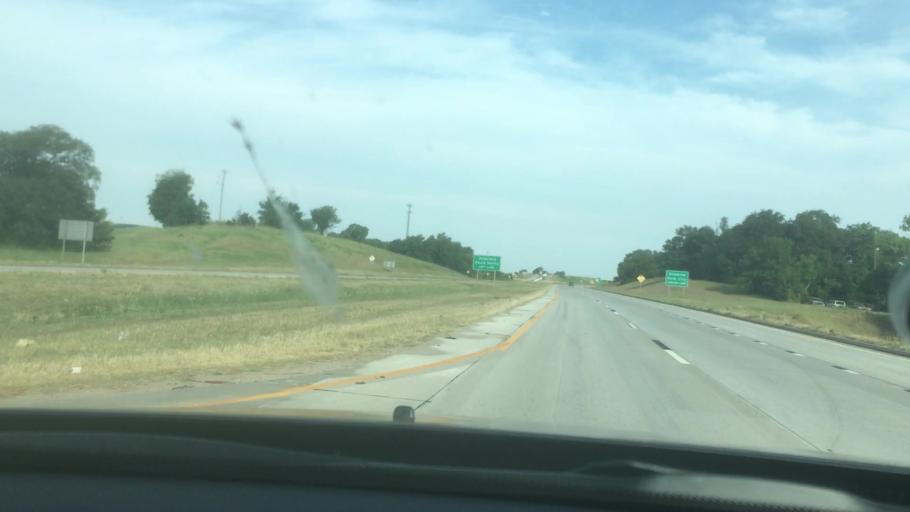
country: US
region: Oklahoma
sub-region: Pontotoc County
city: Ada
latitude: 34.7819
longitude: -96.7162
